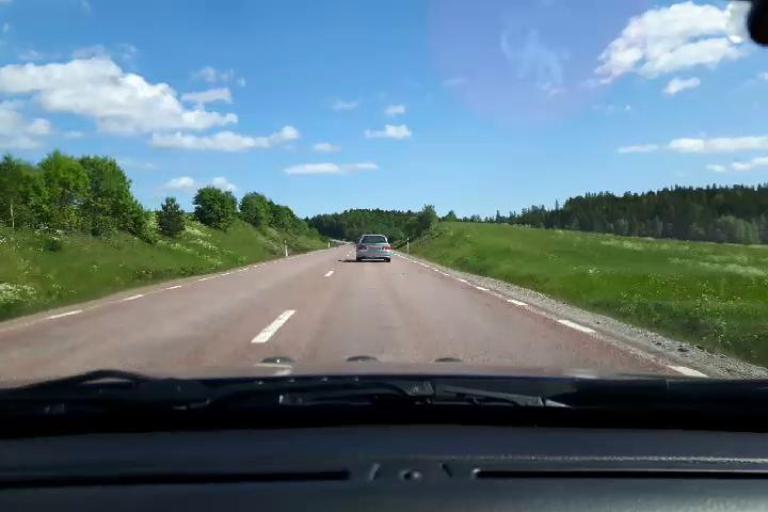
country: SE
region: Gaevleborg
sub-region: Hudiksvalls Kommun
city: Sorforsa
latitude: 61.7439
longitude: 16.8526
